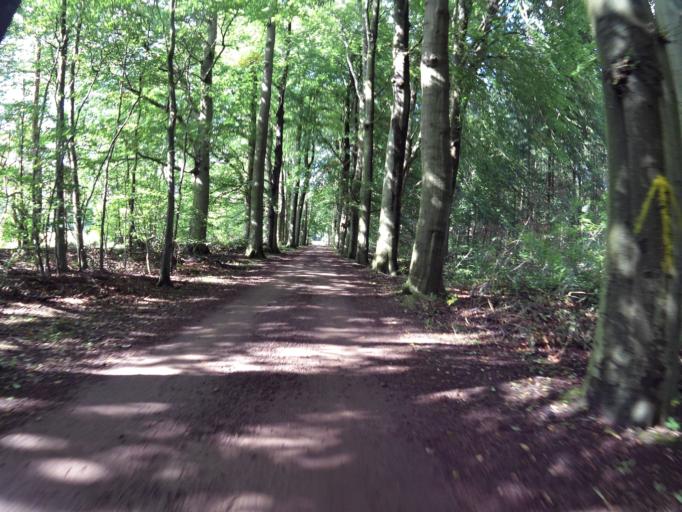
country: NL
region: Utrecht
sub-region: Gemeente Soest
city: Soest
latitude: 52.1777
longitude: 5.2459
